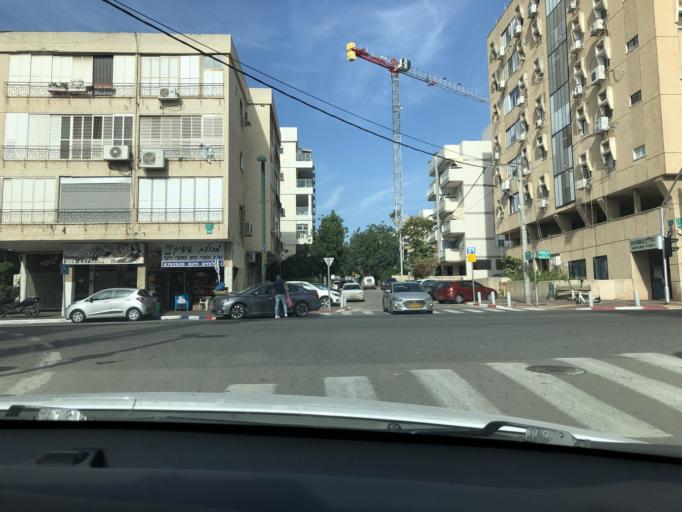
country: IL
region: Tel Aviv
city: Bene Beraq
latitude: 32.0700
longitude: 34.8274
